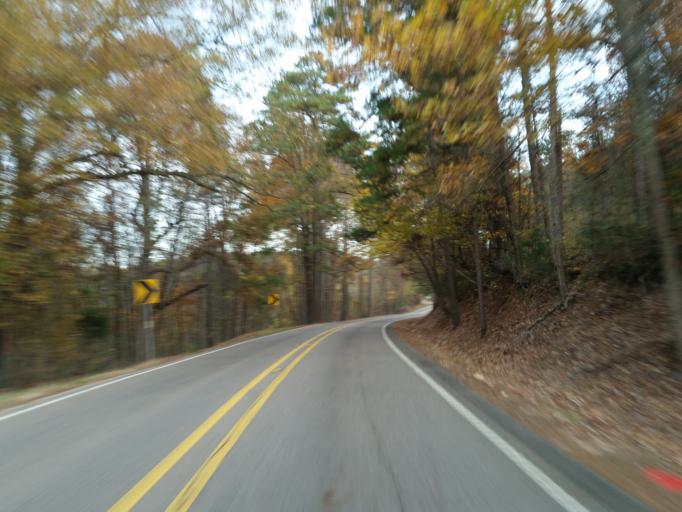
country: US
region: Mississippi
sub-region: Lauderdale County
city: Marion
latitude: 32.4115
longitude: -88.5707
